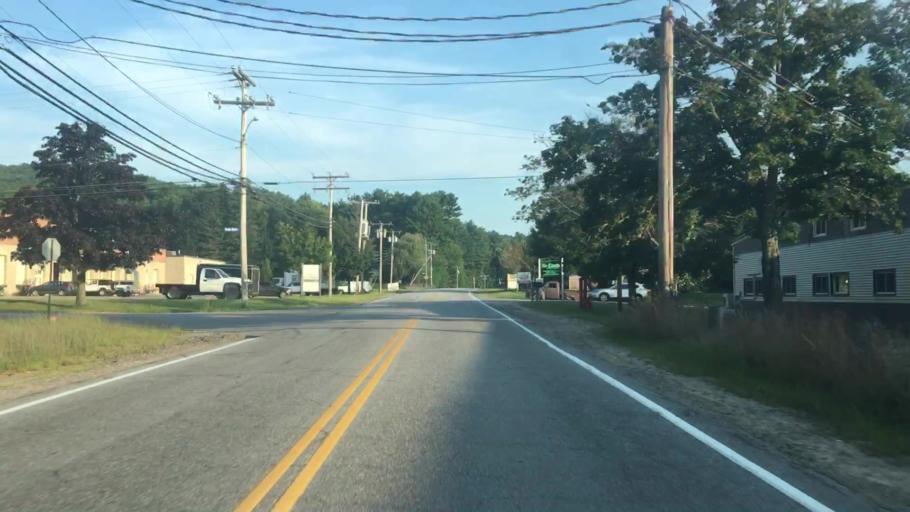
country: US
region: New Hampshire
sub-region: Belknap County
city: Laconia
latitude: 43.5099
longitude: -71.4516
